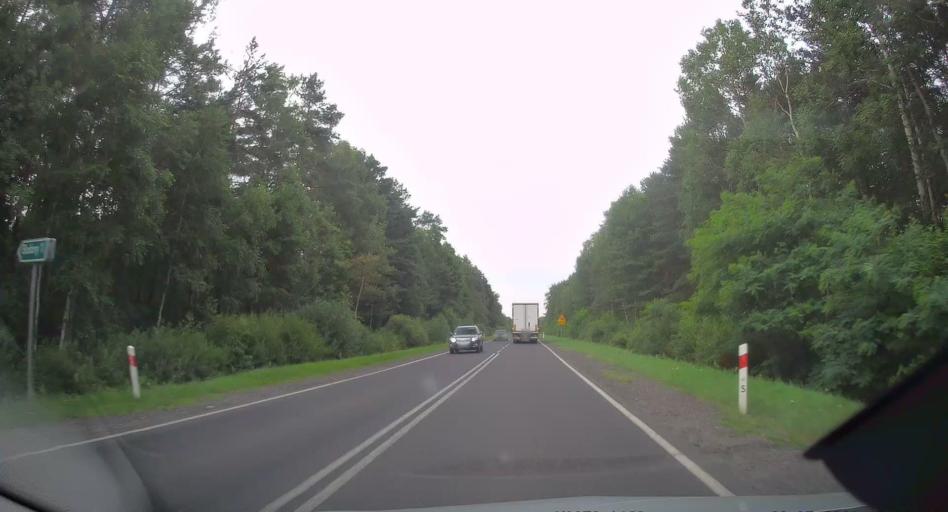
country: PL
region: Lodz Voivodeship
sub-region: Powiat radomszczanski
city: Plawno
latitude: 51.0105
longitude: 19.4209
